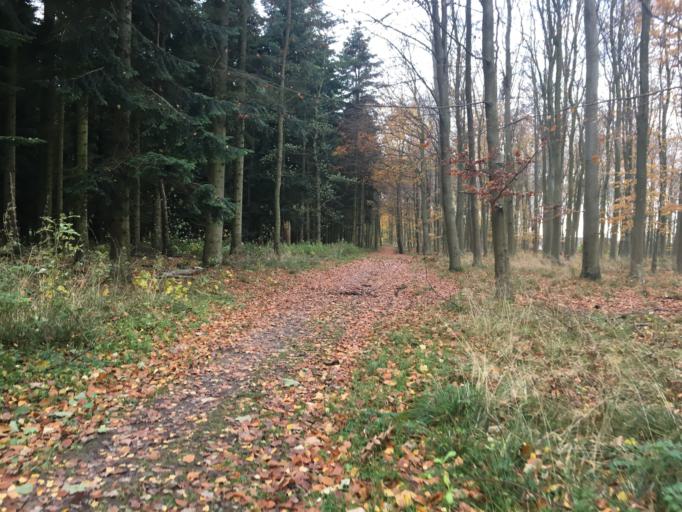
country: DK
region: South Denmark
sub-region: Faaborg-Midtfyn Kommune
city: Faaborg
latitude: 55.0769
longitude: 10.2249
